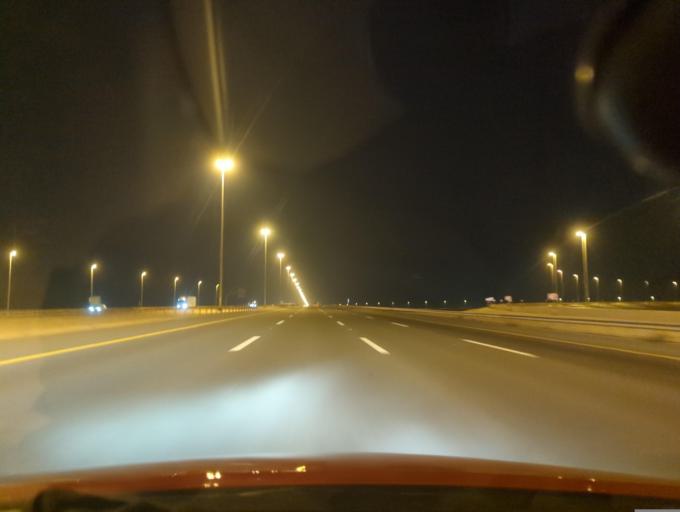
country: AE
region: Abu Dhabi
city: Abu Dhabi
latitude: 24.4657
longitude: 54.7498
